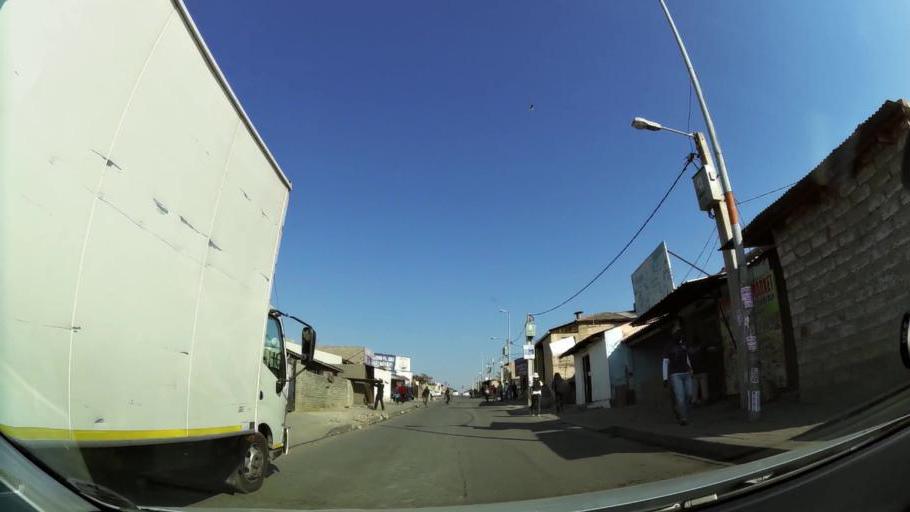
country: ZA
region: Gauteng
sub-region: City of Johannesburg Metropolitan Municipality
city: Modderfontein
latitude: -26.1060
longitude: 28.1069
